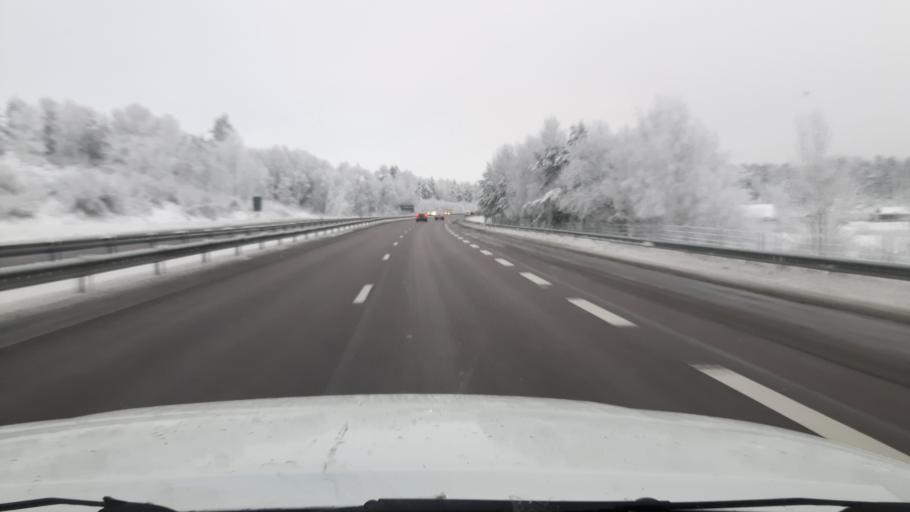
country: SE
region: Halland
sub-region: Kungsbacka Kommun
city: Kungsbacka
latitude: 57.4732
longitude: 12.0536
